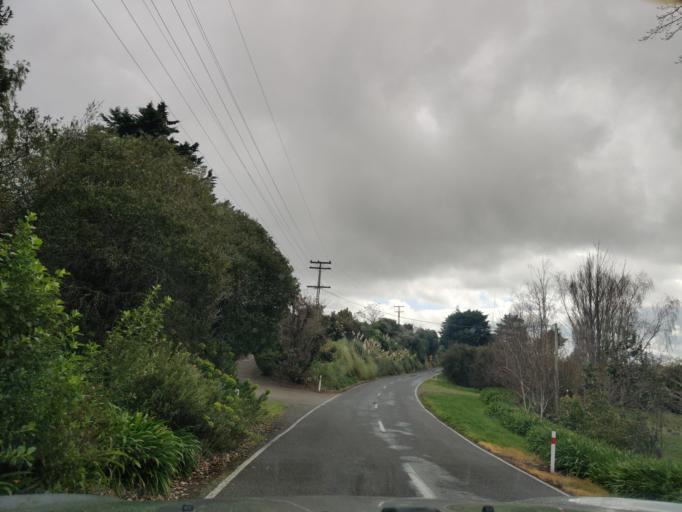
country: NZ
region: Hawke's Bay
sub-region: Hastings District
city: Hastings
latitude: -39.6868
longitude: 176.8982
